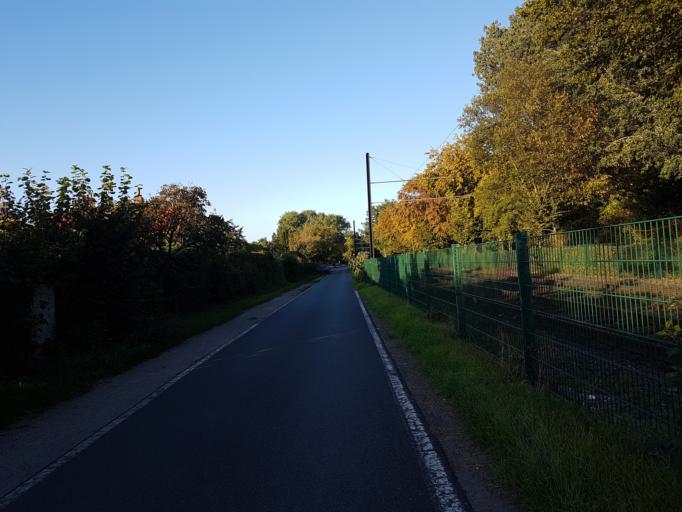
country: DE
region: Lower Saxony
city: Langenhagen
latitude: 52.4178
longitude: 9.7545
